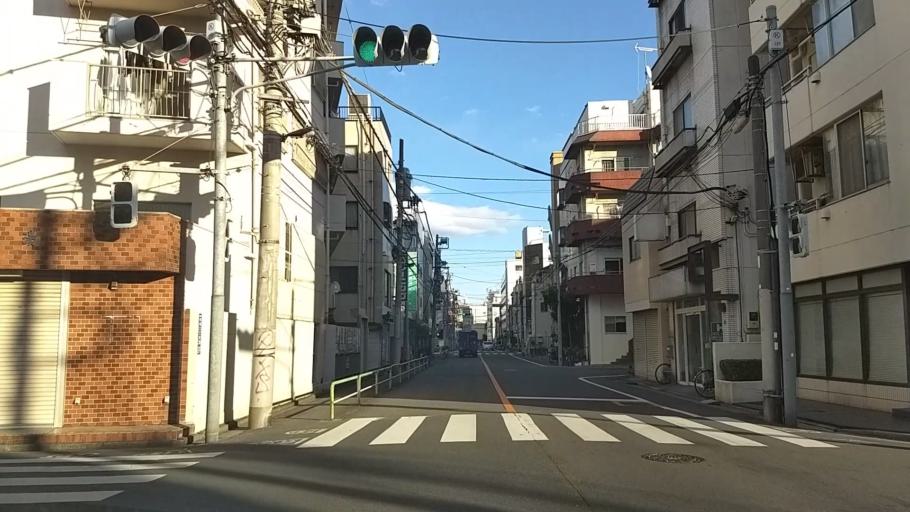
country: JP
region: Saitama
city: Kawaguchi
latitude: 35.7476
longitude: 139.7116
